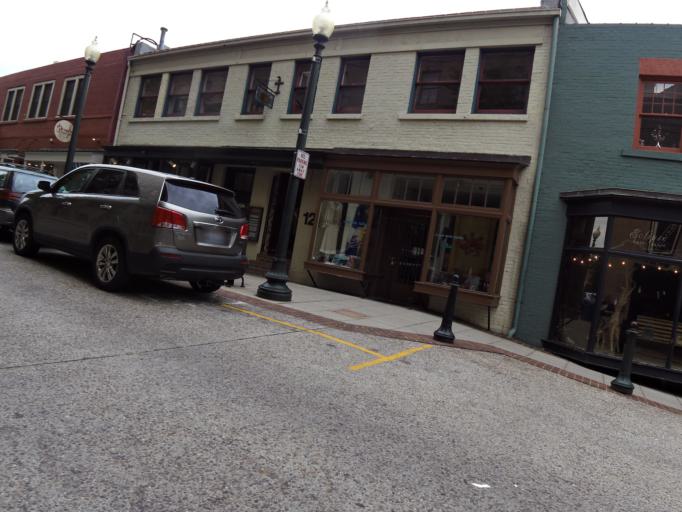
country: US
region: North Carolina
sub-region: Buncombe County
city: Asheville
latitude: 35.5948
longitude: -82.5552
